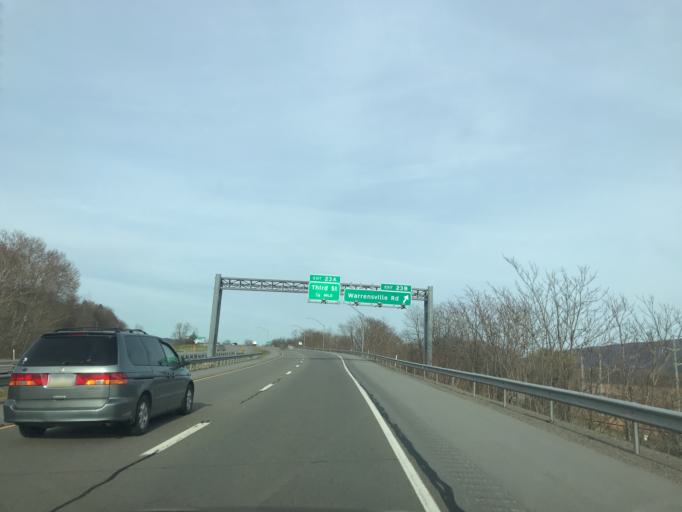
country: US
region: Pennsylvania
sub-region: Lycoming County
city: Kenmar
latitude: 41.2455
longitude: -76.9520
